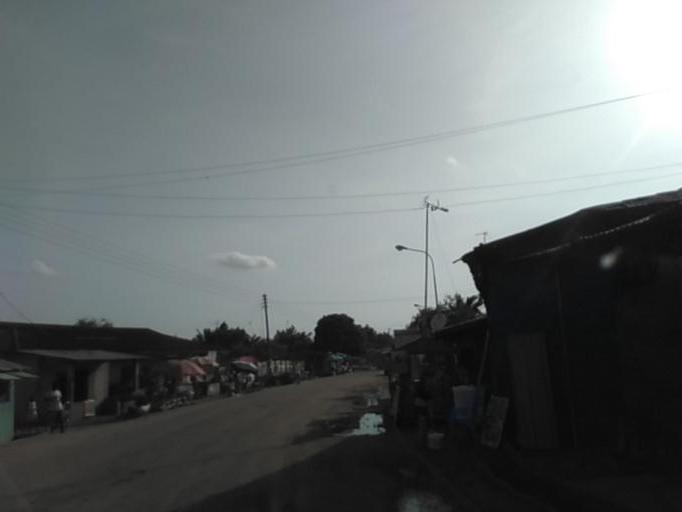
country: GH
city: Akropong
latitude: 6.1009
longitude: 0.1280
